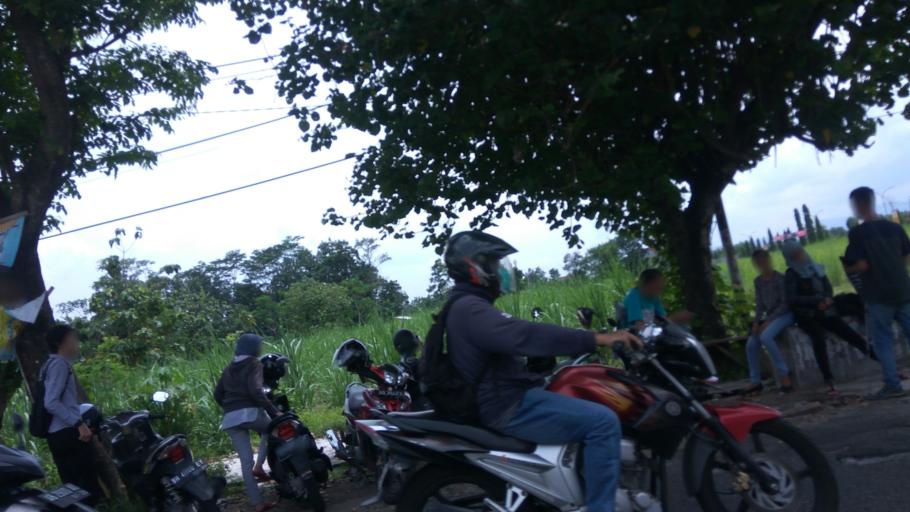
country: ID
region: Daerah Istimewa Yogyakarta
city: Depok
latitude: -7.7494
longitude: 110.4194
